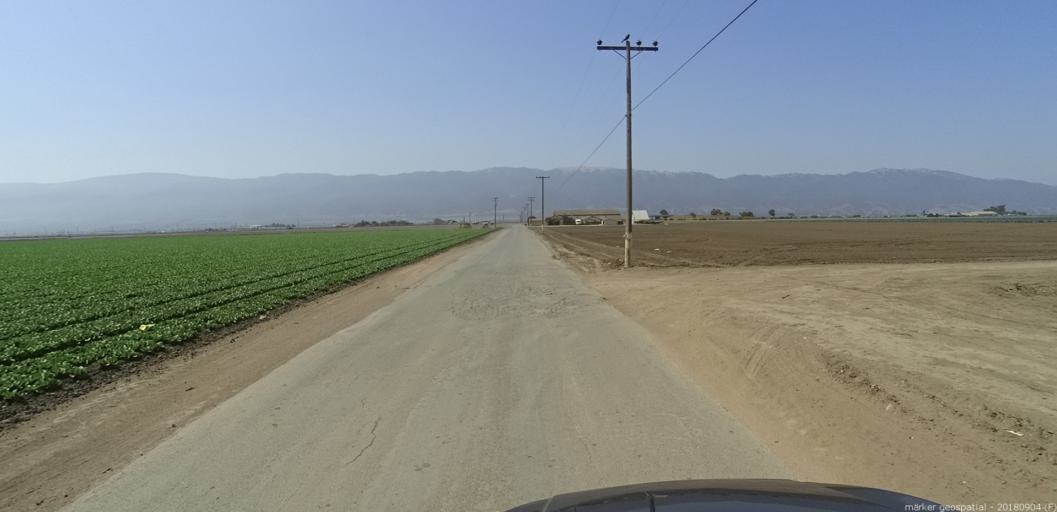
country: US
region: California
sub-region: Monterey County
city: Gonzales
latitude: 36.5265
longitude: -121.4561
